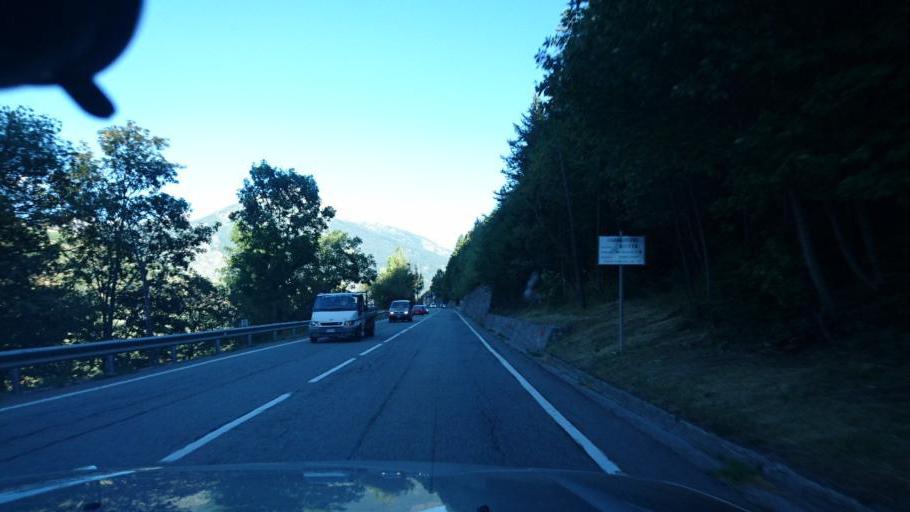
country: IT
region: Aosta Valley
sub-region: Valle d'Aosta
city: Allein
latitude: 45.8041
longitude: 7.2578
